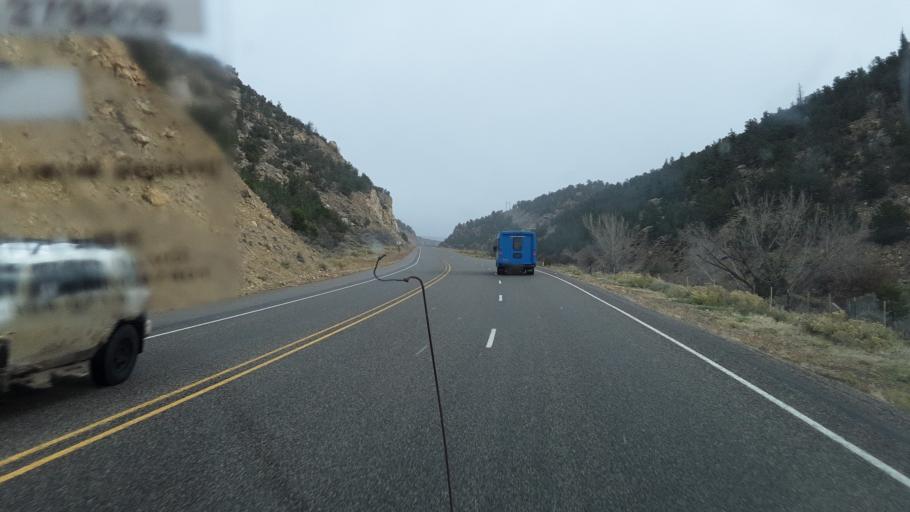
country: US
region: New Mexico
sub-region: Rio Arriba County
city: Tierra Amarilla
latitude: 36.4150
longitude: -106.4820
